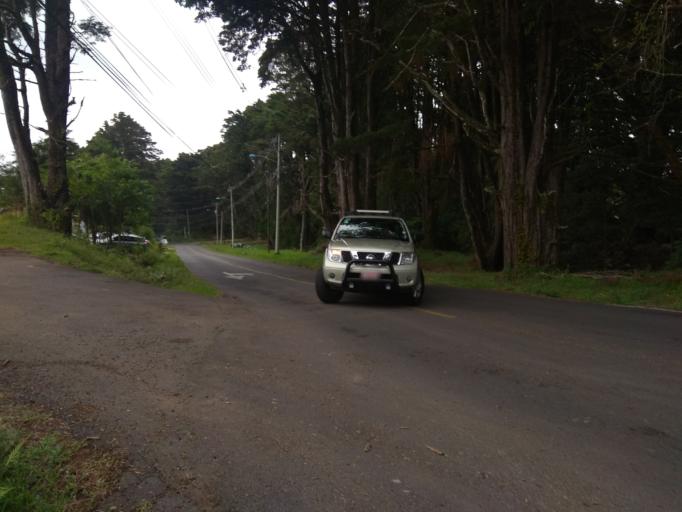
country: CR
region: Heredia
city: San Josecito
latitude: 10.0686
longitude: -84.0843
